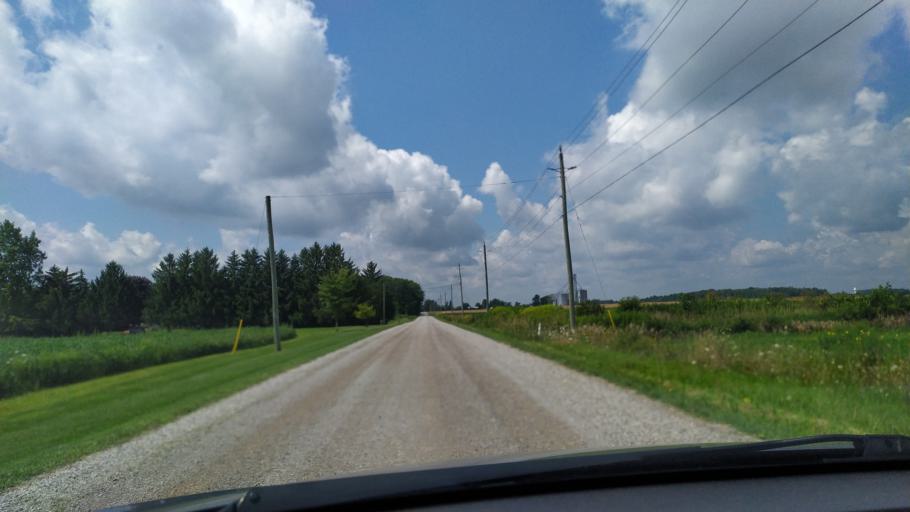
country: CA
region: Ontario
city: London
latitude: 43.0805
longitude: -81.3297
